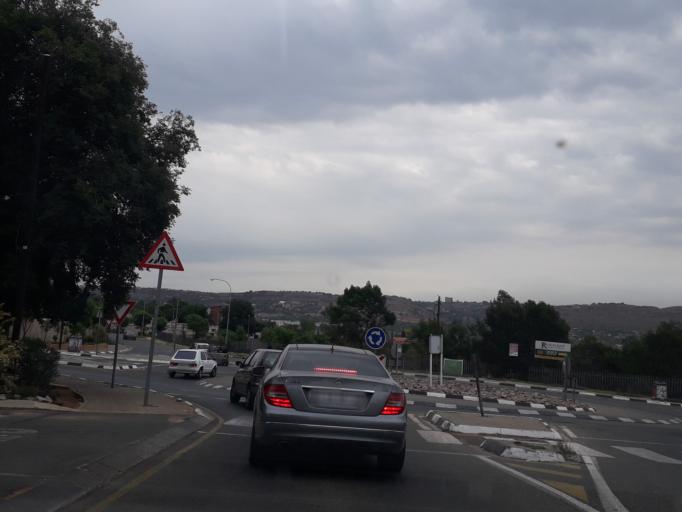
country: ZA
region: Gauteng
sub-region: City of Johannesburg Metropolitan Municipality
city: Roodepoort
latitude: -26.1100
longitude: 27.9167
